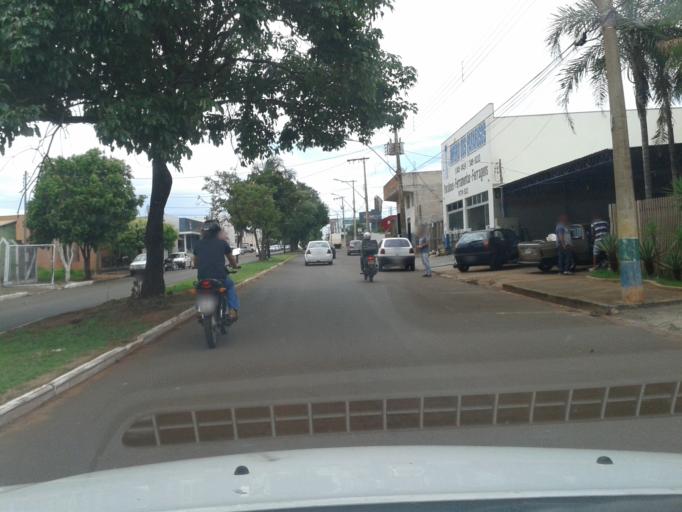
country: BR
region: Minas Gerais
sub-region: Iturama
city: Iturama
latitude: -19.7219
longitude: -50.1947
